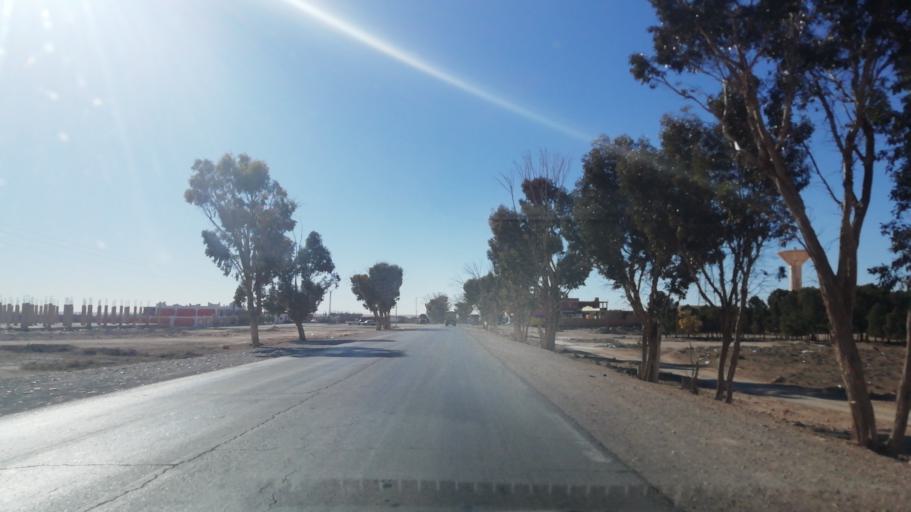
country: DZ
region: Saida
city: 'Ain el Hadjar
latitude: 34.1587
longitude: 0.0711
